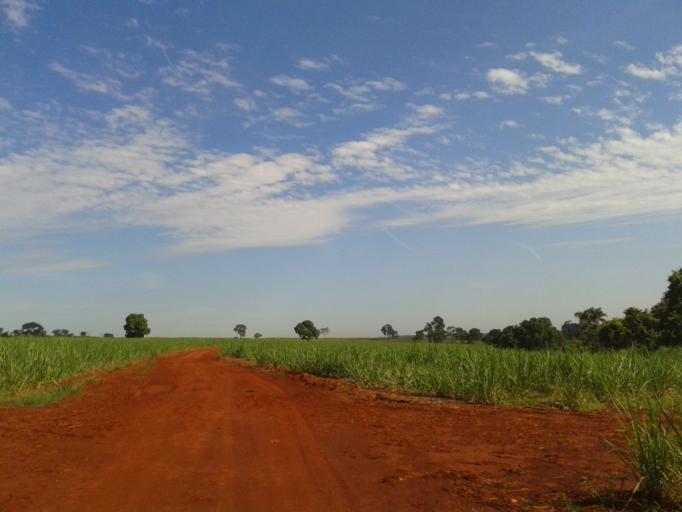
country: BR
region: Minas Gerais
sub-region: Centralina
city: Centralina
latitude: -18.6339
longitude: -49.2593
